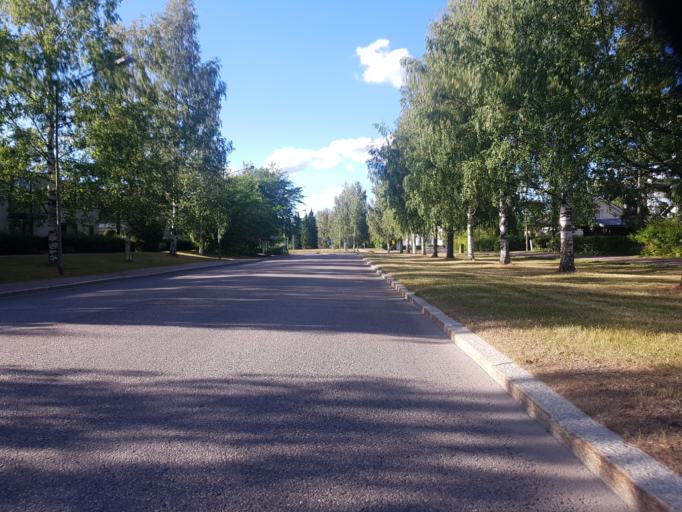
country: FI
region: Uusimaa
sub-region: Helsinki
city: Vantaa
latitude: 60.2762
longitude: 24.9905
